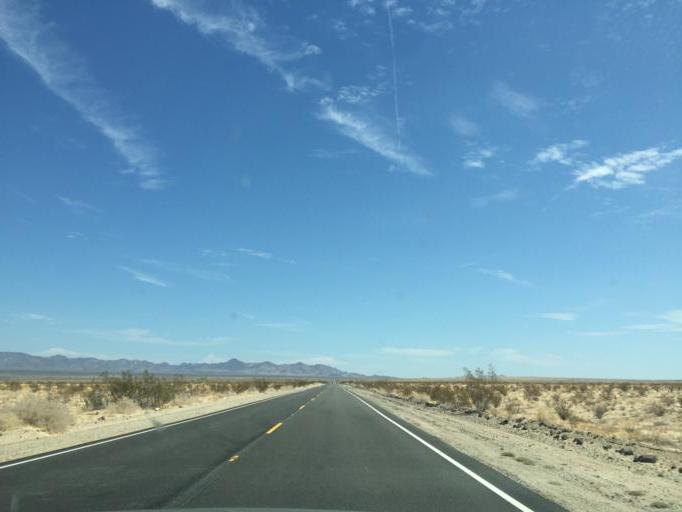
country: US
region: California
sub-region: Riverside County
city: Mesa Verde
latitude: 34.0989
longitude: -115.0119
